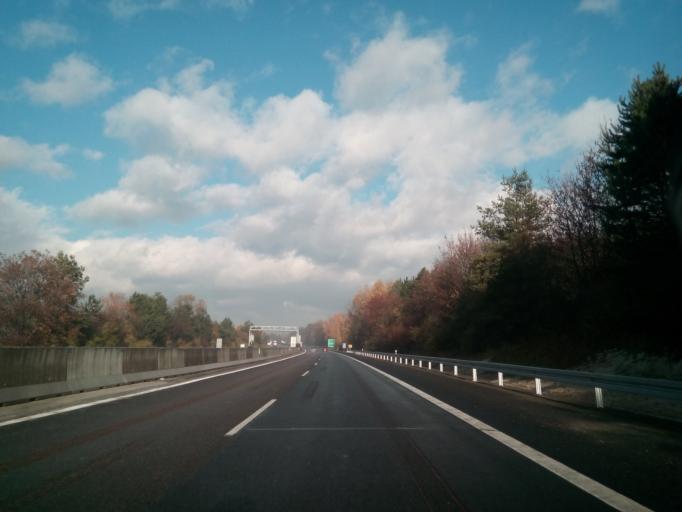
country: SK
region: Presovsky
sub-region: Okres Presov
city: Presov
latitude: 48.9419
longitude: 21.2588
